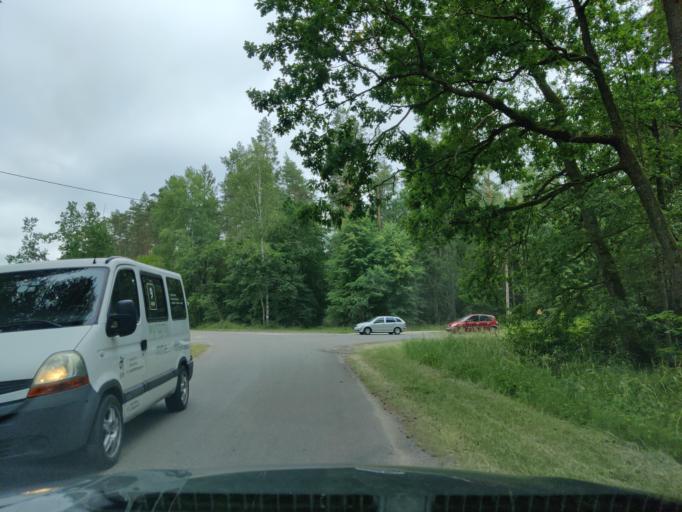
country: PL
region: Warmian-Masurian Voivodeship
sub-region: Powiat piski
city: Ruciane-Nida
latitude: 53.5537
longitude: 21.4758
